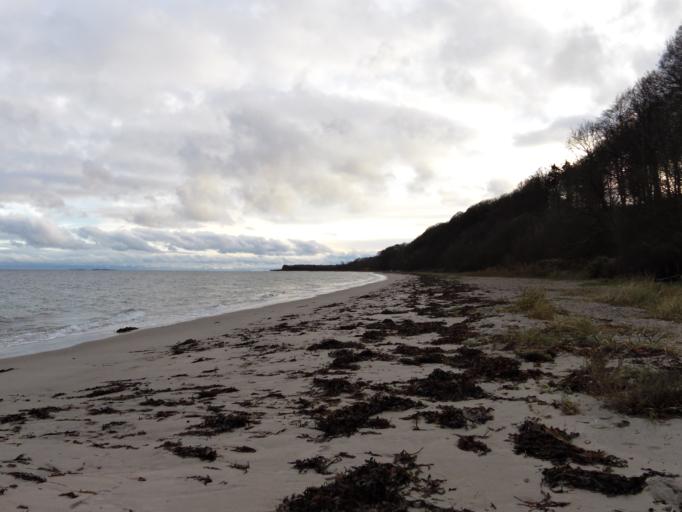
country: DK
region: Central Jutland
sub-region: Arhus Kommune
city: Beder
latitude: 56.0678
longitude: 10.2578
